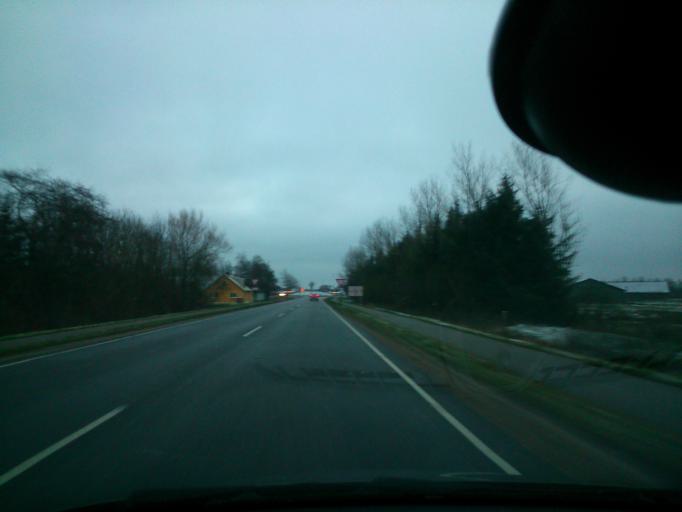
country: DK
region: Central Jutland
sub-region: Ringkobing-Skjern Kommune
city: Tarm
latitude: 55.9201
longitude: 8.5165
